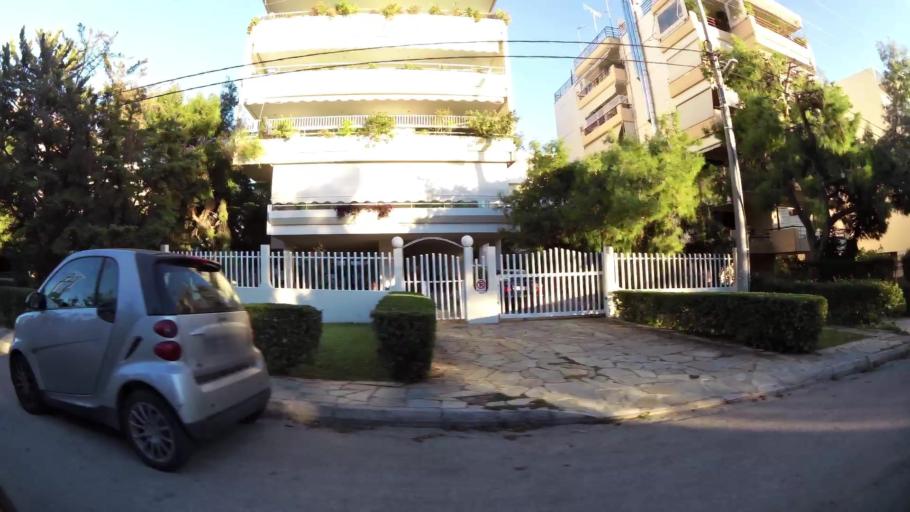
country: GR
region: Attica
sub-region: Nomarchia Athinas
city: Glyfada
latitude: 37.8718
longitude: 23.7496
